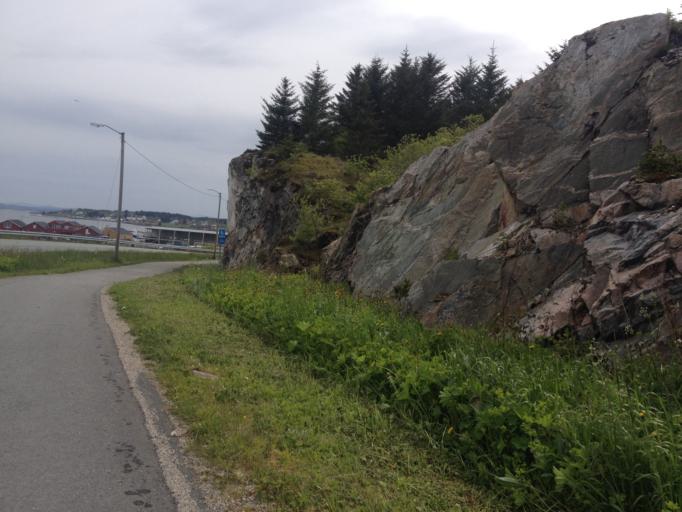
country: NO
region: Sor-Trondelag
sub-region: Froya
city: Sistranda
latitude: 63.7406
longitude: 8.8367
